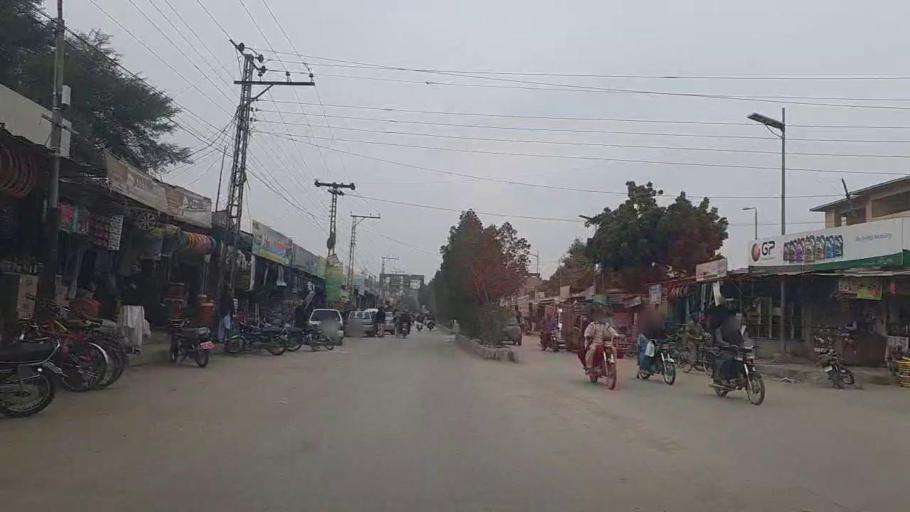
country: PK
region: Sindh
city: Nawabshah
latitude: 26.2503
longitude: 68.4056
